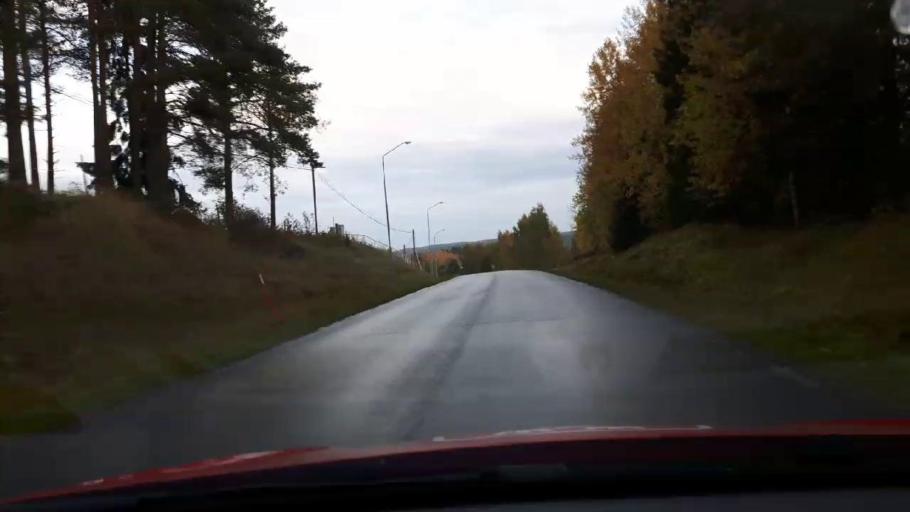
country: SE
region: Jaemtland
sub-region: OEstersunds Kommun
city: Lit
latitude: 63.3182
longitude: 14.8251
